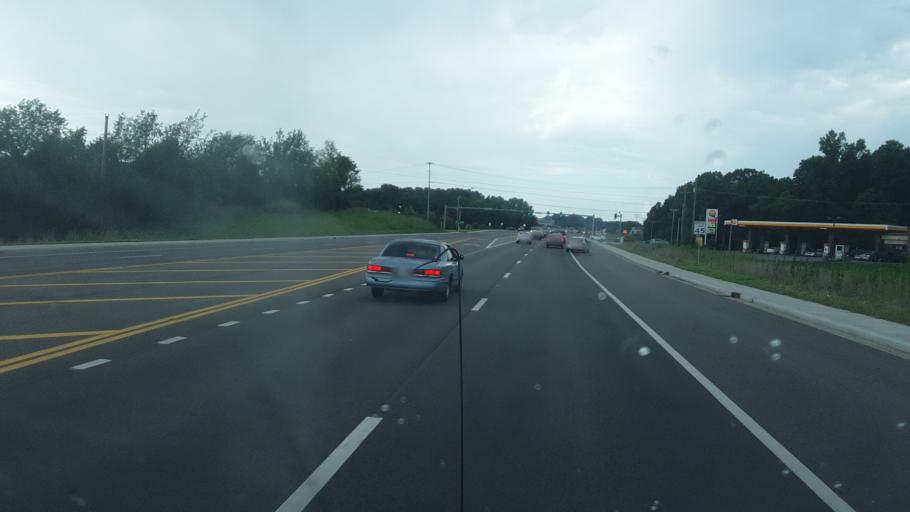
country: US
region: Tennessee
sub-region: Montgomery County
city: Clarksville
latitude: 36.5591
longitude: -87.2881
